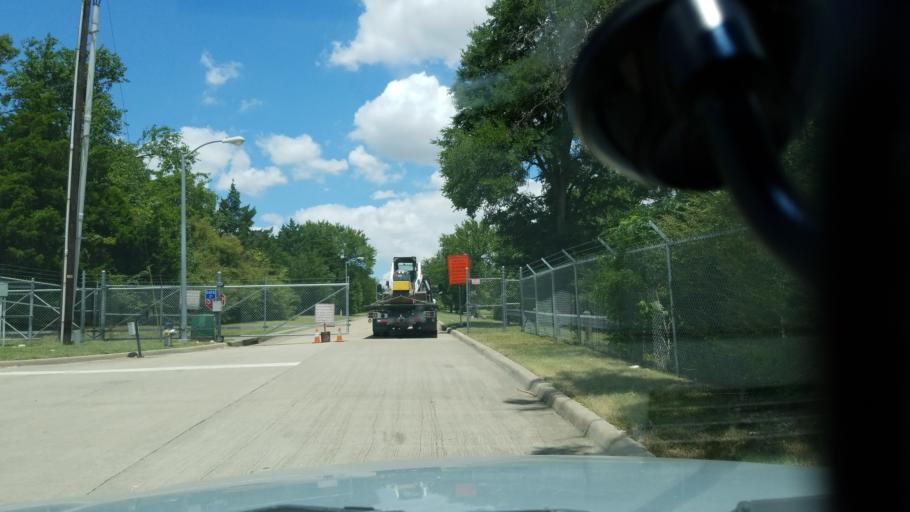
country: US
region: Texas
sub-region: Dallas County
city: Duncanville
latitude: 32.6734
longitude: -96.8743
